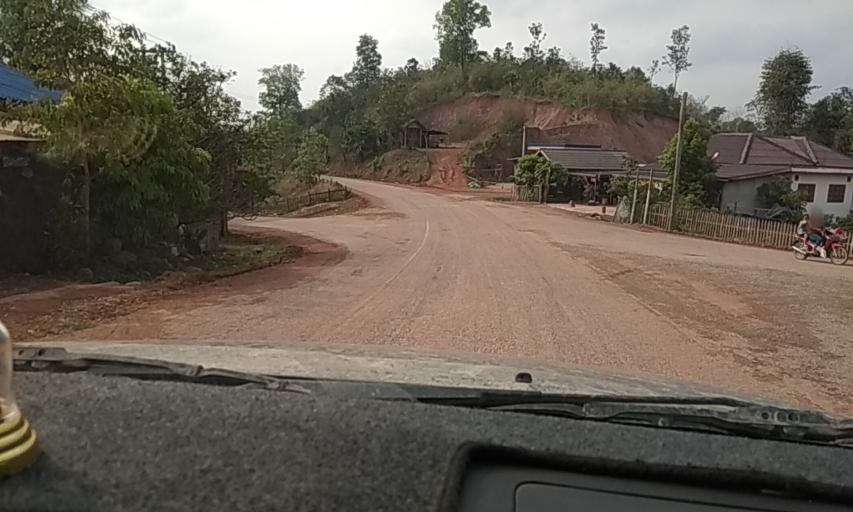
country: TH
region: Nan
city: Mae Charim
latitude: 18.4029
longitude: 101.1767
